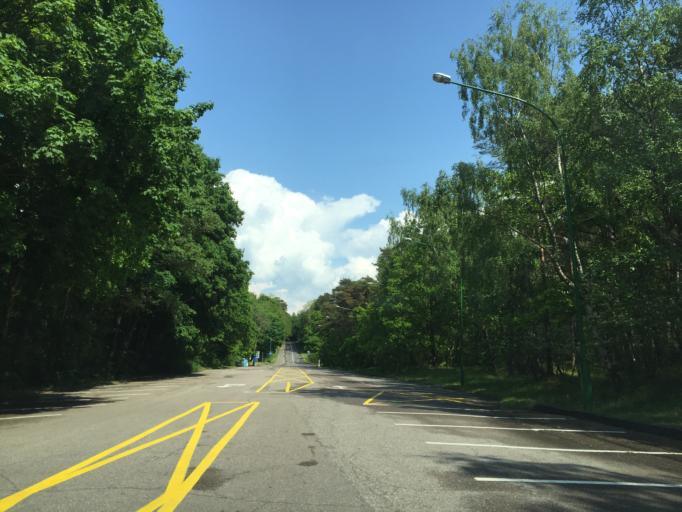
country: LT
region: Klaipedos apskritis
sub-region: Klaipeda
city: Klaipeda
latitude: 55.7658
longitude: 21.0846
